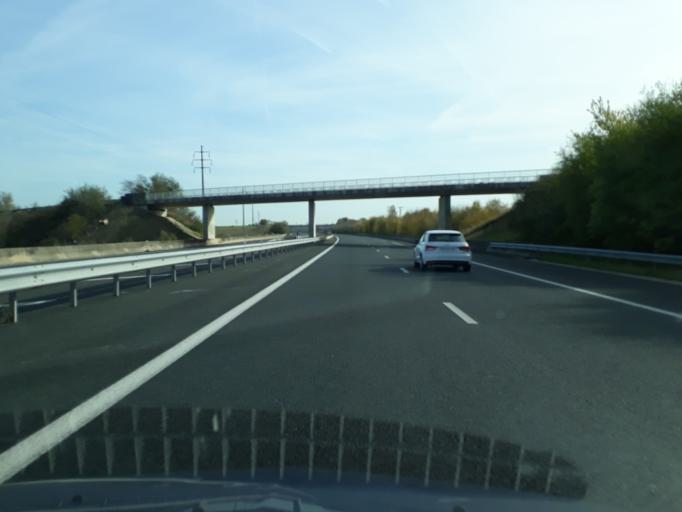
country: FR
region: Champagne-Ardenne
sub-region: Departement de l'Aube
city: Saint-Germain
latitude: 48.2383
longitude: 4.0097
